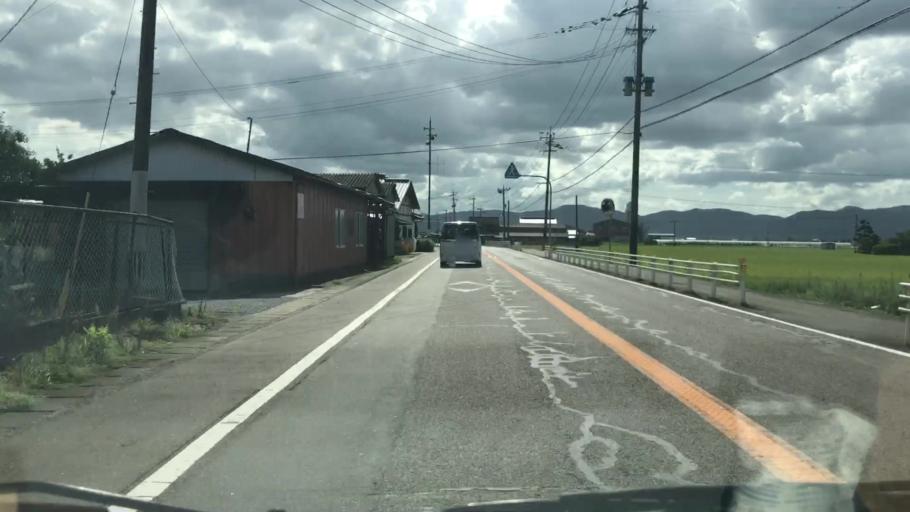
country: JP
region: Saga Prefecture
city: Kashima
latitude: 33.1685
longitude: 130.1781
